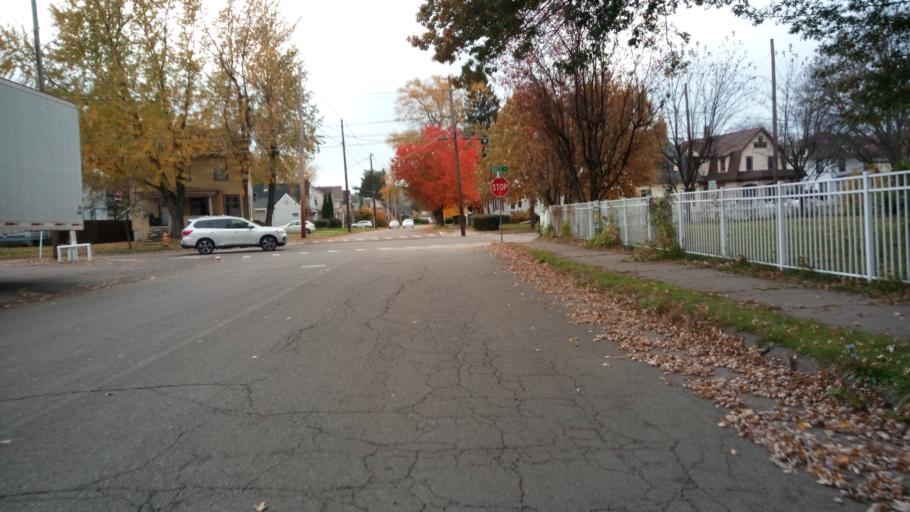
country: US
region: New York
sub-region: Chemung County
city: Elmira
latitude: 42.0795
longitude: -76.7899
